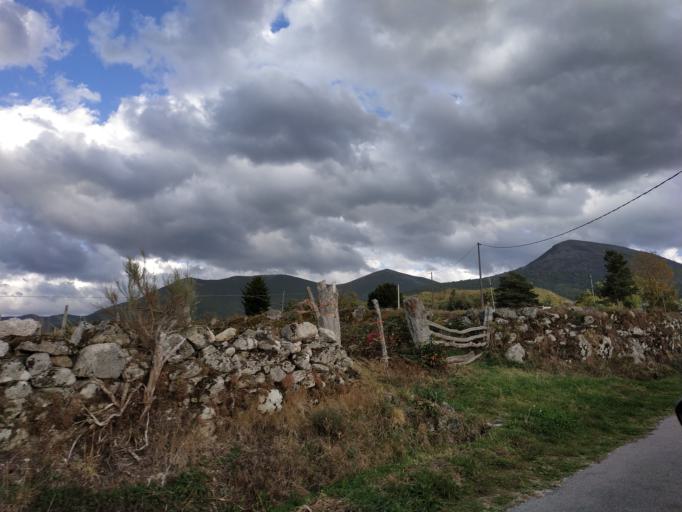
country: ES
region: Castille and Leon
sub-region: Provincia de Leon
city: Candin
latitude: 42.8575
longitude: -6.8782
